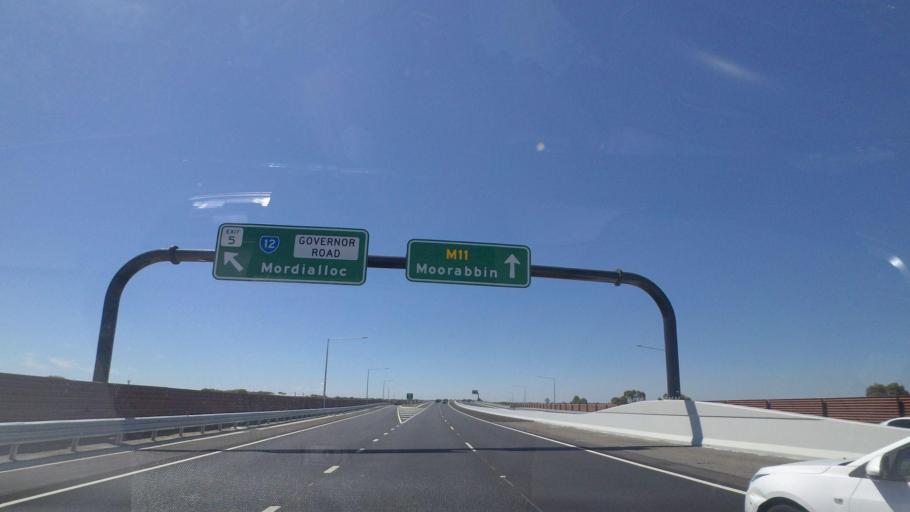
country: AU
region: Victoria
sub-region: Kingston
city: Waterways
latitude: -38.0139
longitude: 145.1237
